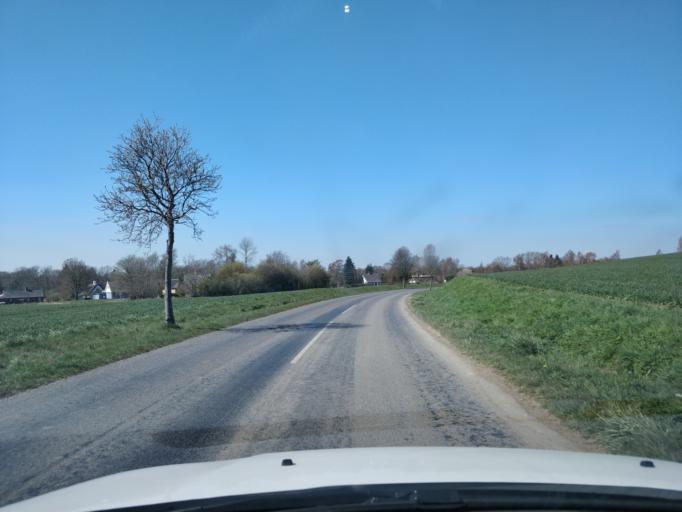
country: DK
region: Zealand
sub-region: Vordingborg Kommune
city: Stege
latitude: 54.9865
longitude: 12.3870
